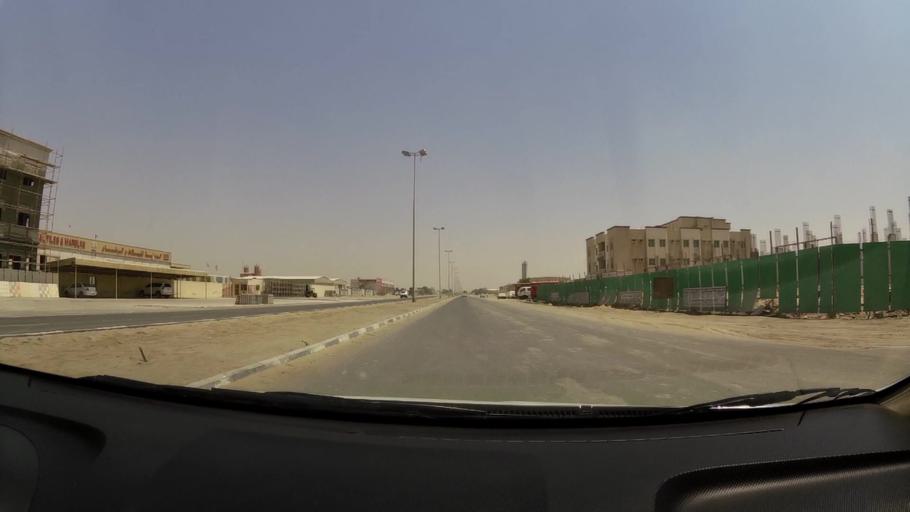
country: AE
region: Umm al Qaywayn
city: Umm al Qaywayn
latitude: 25.5100
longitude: 55.5585
